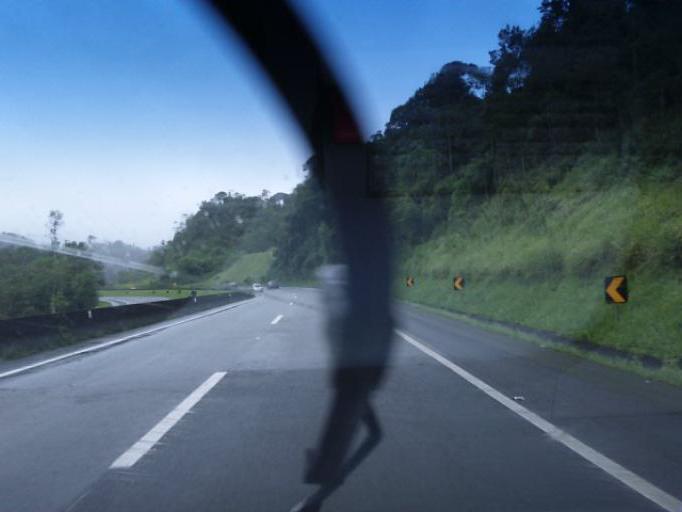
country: BR
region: Parana
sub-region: Antonina
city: Antonina
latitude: -25.0999
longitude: -48.6907
